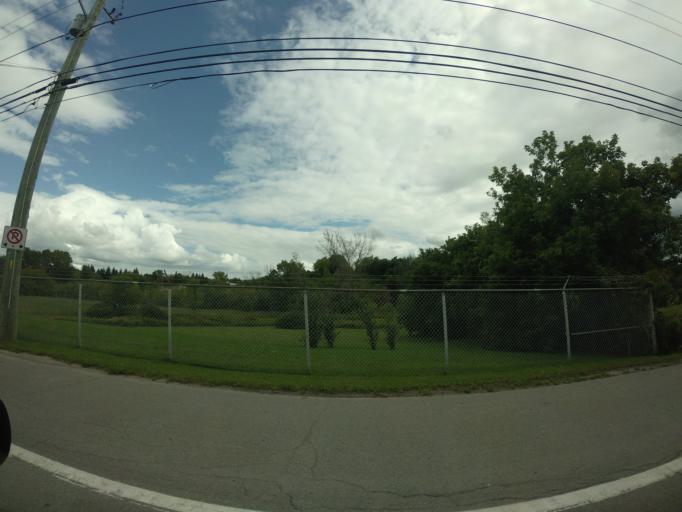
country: CA
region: Quebec
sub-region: Outaouais
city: Gatineau
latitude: 45.4580
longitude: -75.5653
